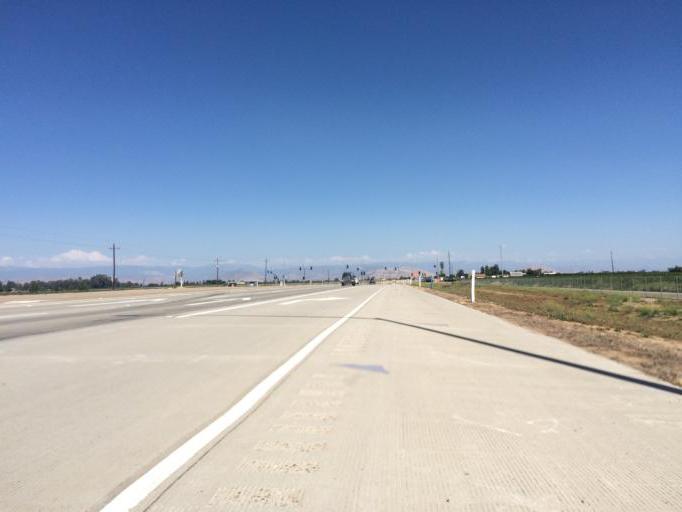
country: US
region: California
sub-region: Fresno County
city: Sunnyside
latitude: 36.7369
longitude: -119.6489
